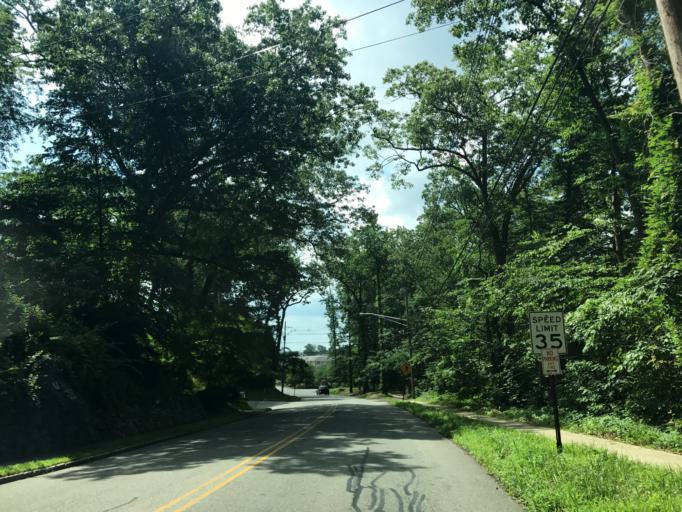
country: US
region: New Jersey
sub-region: Morris County
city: Mountain Lakes
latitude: 40.9003
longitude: -74.4213
